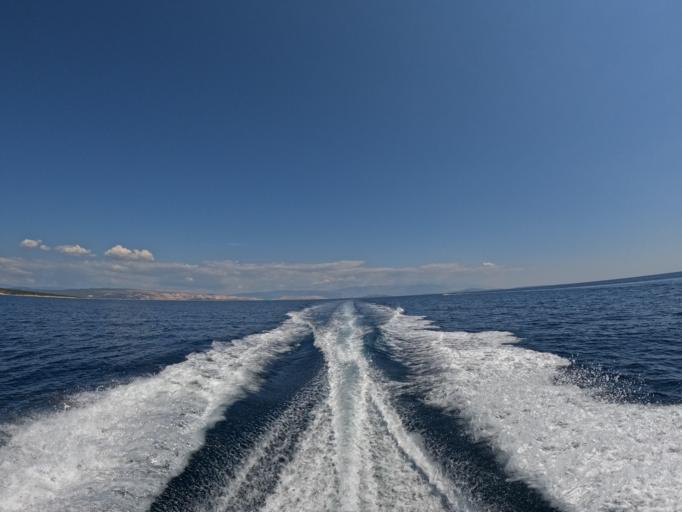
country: HR
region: Primorsko-Goranska
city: Cres
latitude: 44.9371
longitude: 14.5040
